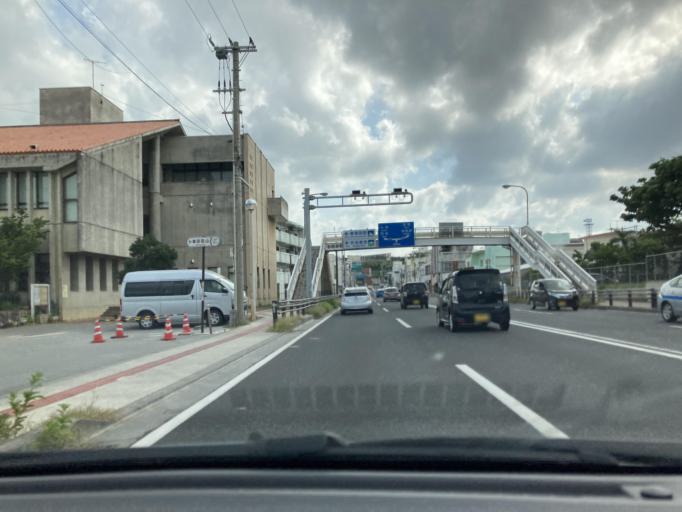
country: JP
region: Okinawa
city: Ginowan
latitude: 26.2041
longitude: 127.7554
